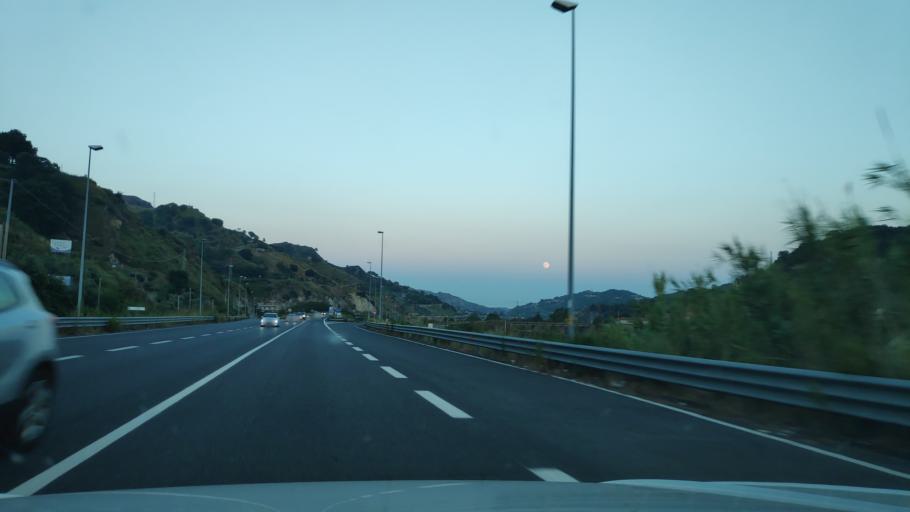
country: IT
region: Calabria
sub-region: Provincia di Reggio Calabria
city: Mammola
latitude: 38.3579
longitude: 16.2323
